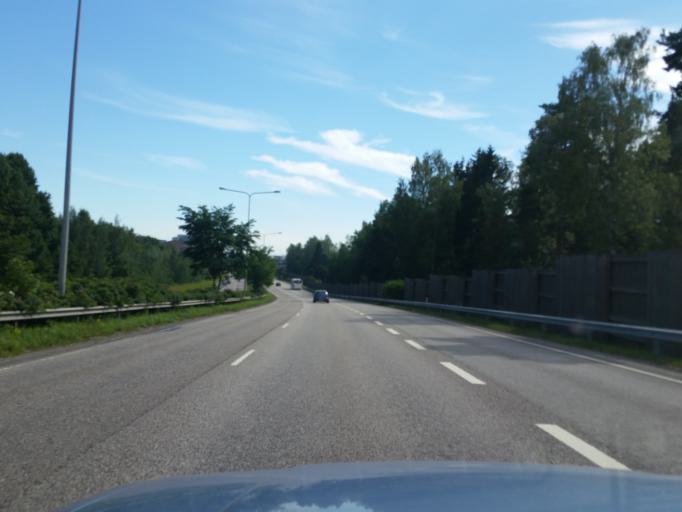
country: FI
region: Uusimaa
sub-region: Helsinki
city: Otaniemi
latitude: 60.1938
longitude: 24.8064
